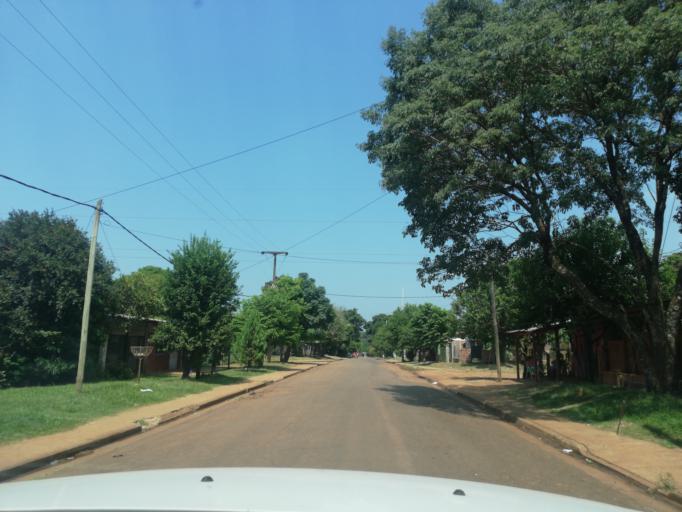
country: AR
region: Misiones
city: Garupa
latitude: -27.4435
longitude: -55.8877
